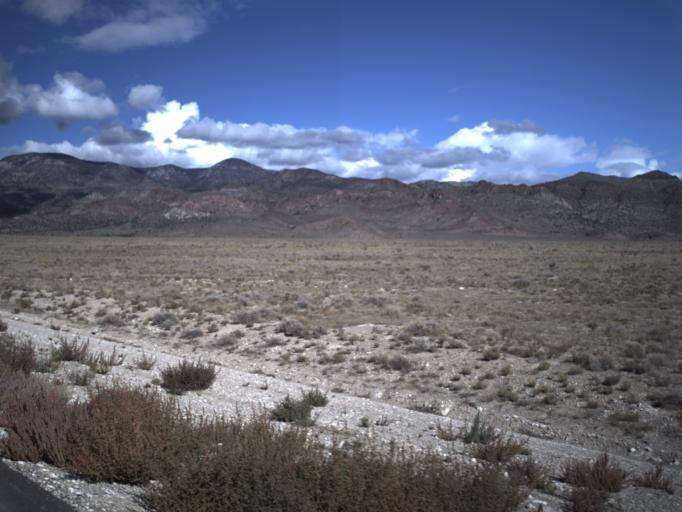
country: US
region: Utah
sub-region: Beaver County
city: Milford
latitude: 38.4904
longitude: -113.4681
